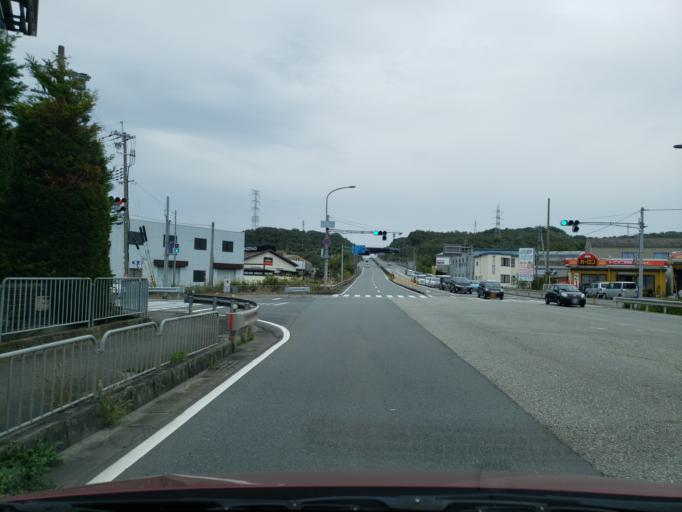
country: JP
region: Hyogo
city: Miki
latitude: 34.8060
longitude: 134.9639
